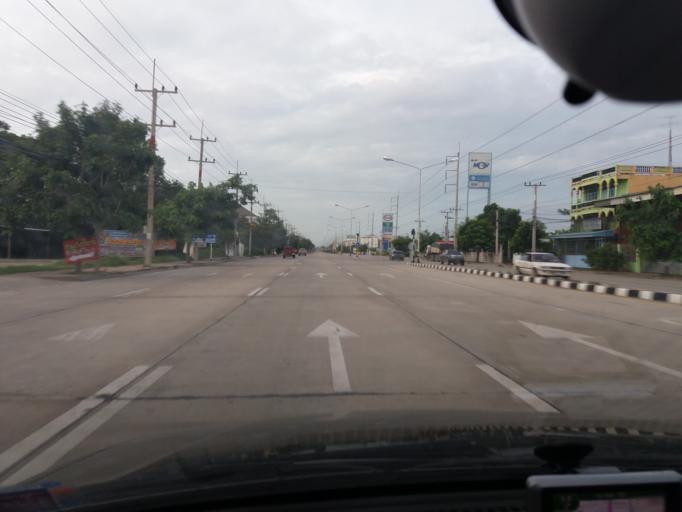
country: TH
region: Suphan Buri
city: U Thong
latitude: 14.3883
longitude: 99.8951
